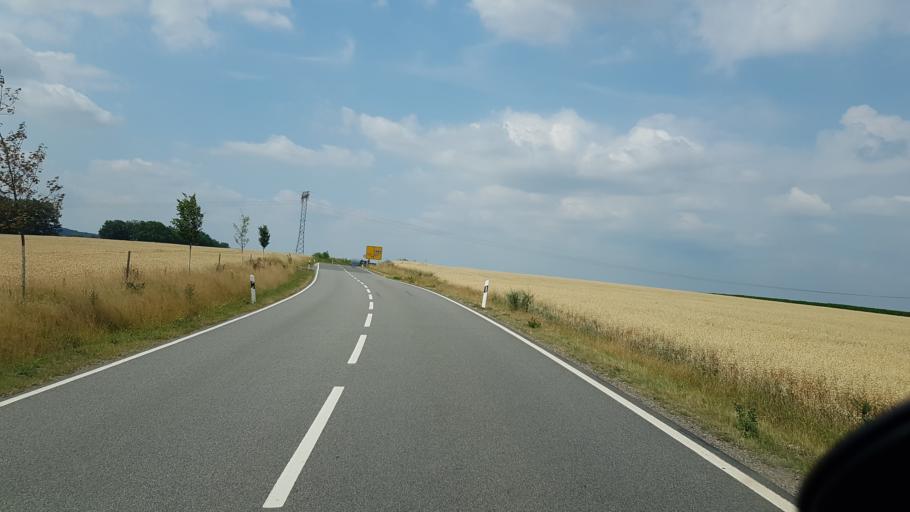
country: DE
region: Saxony
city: Lichtentanne
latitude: 50.6844
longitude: 12.4515
